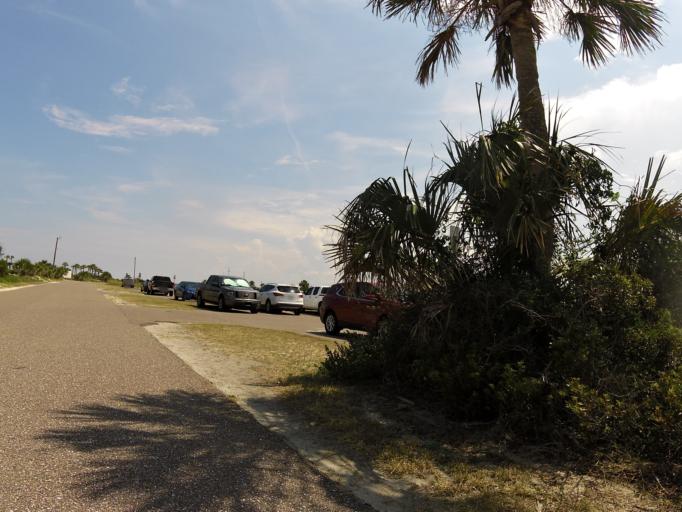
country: US
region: Florida
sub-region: Duval County
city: Atlantic Beach
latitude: 30.4324
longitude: -81.4107
